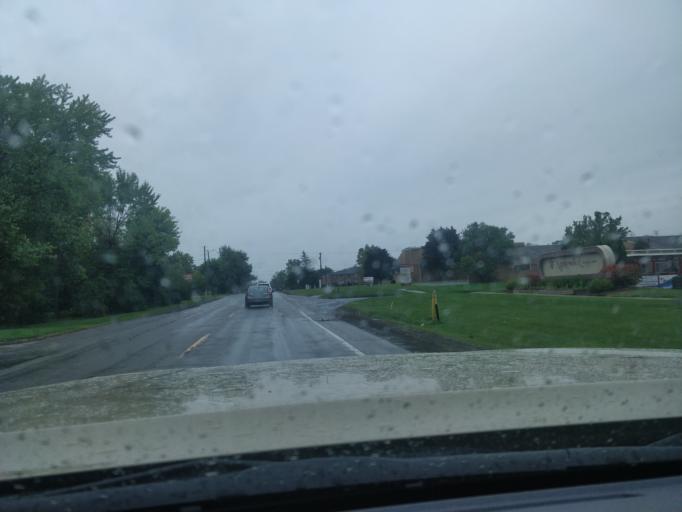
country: US
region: Michigan
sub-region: Wayne County
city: Woodhaven
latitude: 42.1264
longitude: -83.2166
